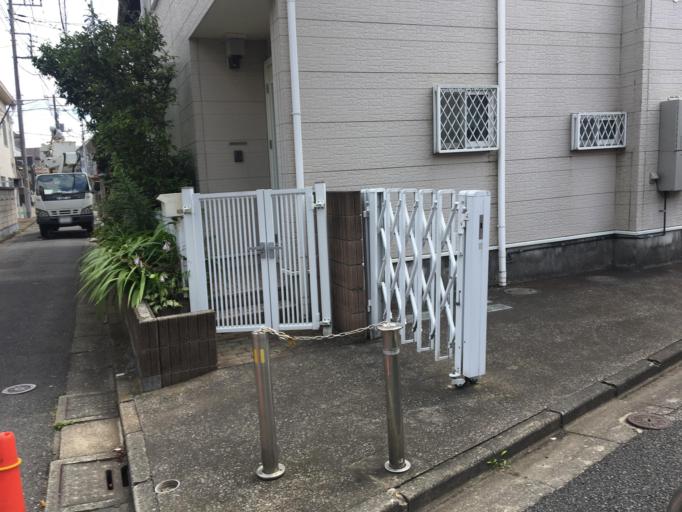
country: JP
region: Chiba
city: Matsudo
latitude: 35.7355
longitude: 139.8493
